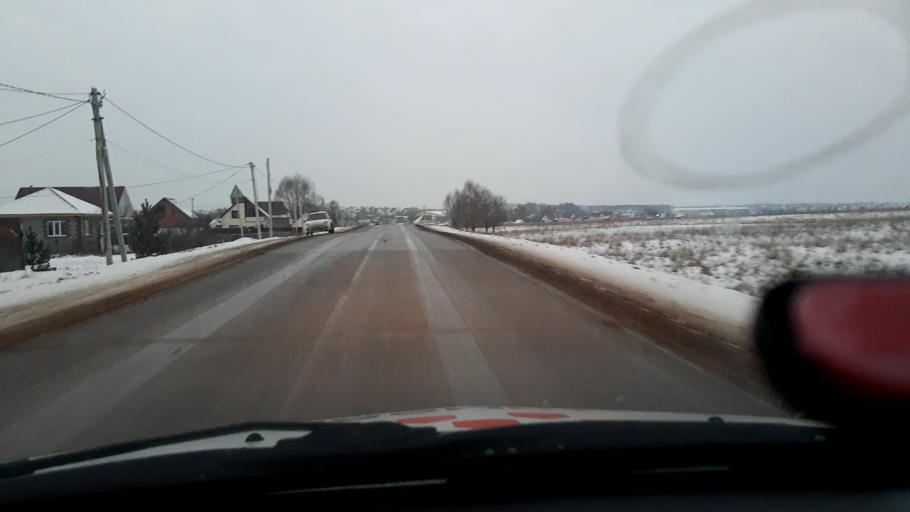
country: RU
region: Bashkortostan
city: Iglino
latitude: 54.8431
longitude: 56.4528
